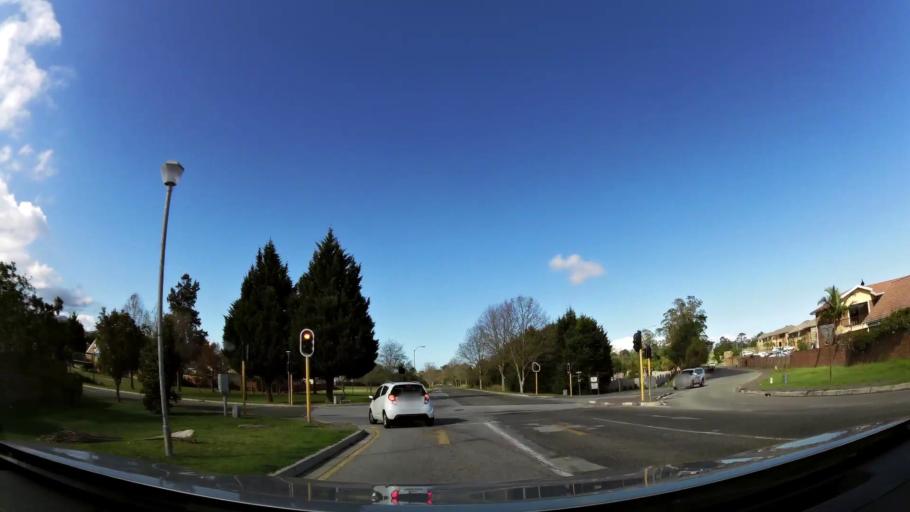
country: ZA
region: Western Cape
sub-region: Eden District Municipality
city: George
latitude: -33.9678
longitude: 22.4911
